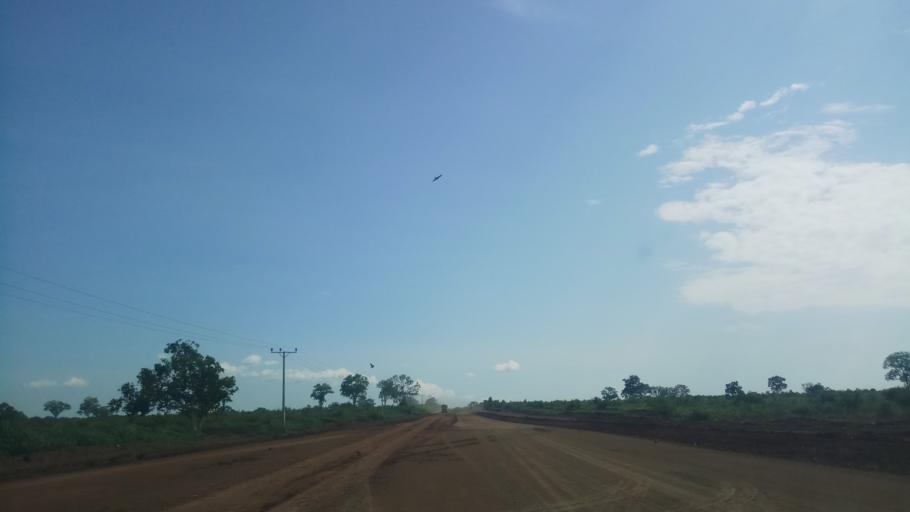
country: ET
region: Gambela
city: Gambela
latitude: 8.1827
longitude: 34.4953
